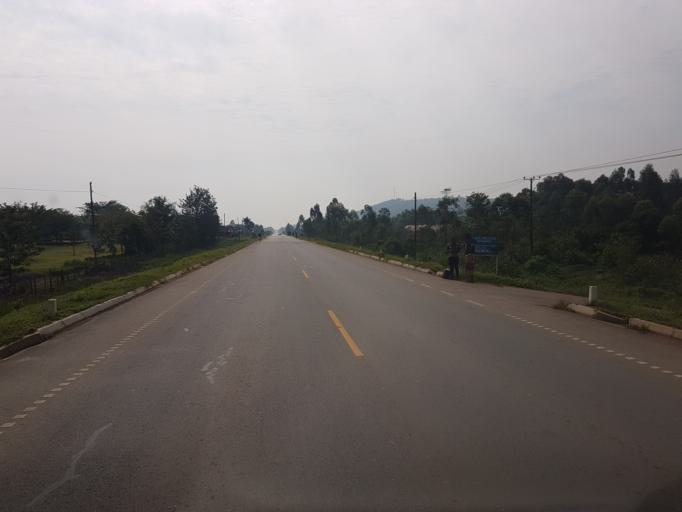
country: UG
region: Western Region
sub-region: Sheema District
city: Kibingo
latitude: -0.6454
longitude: 30.4949
